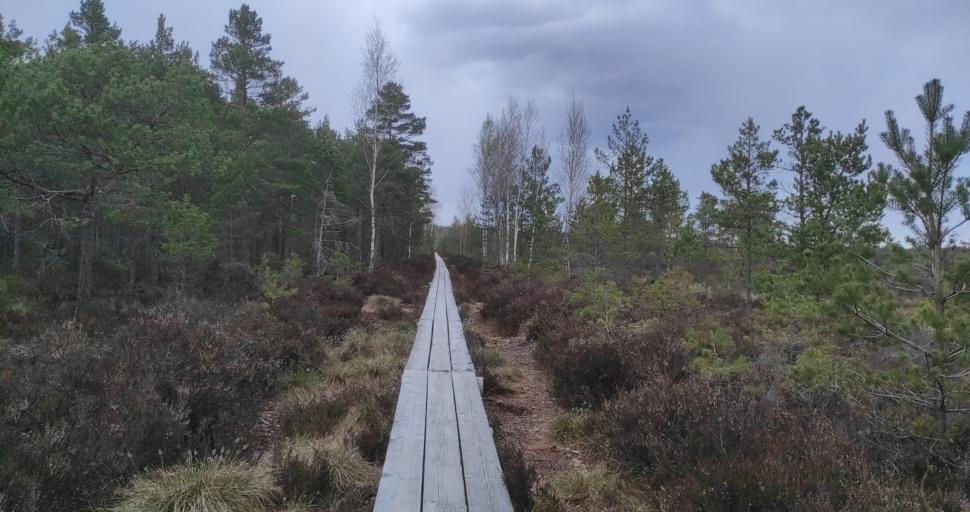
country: LV
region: Dundaga
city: Dundaga
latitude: 57.3499
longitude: 22.1500
